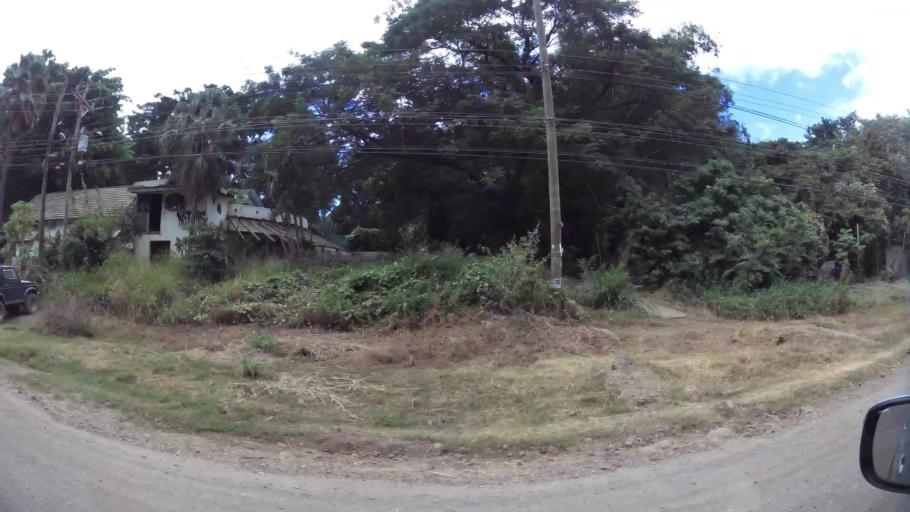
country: CR
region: Guanacaste
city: Santa Cruz
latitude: 10.2969
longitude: -85.8404
